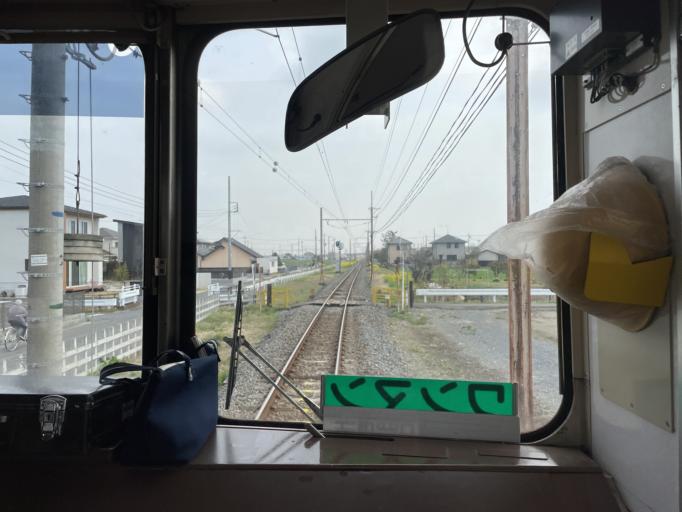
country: JP
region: Saitama
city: Kumagaya
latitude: 36.1363
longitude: 139.4070
